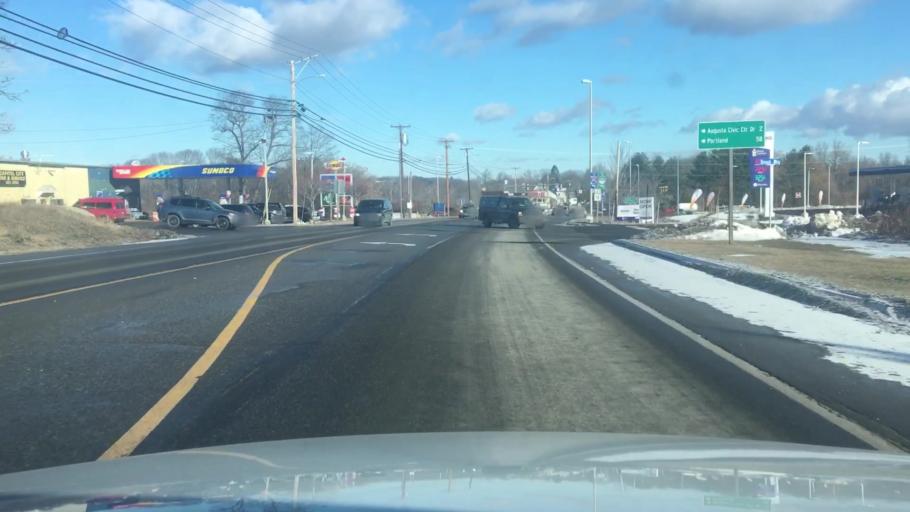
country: US
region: Maine
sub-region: Kennebec County
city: Augusta
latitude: 44.3317
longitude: -69.7620
